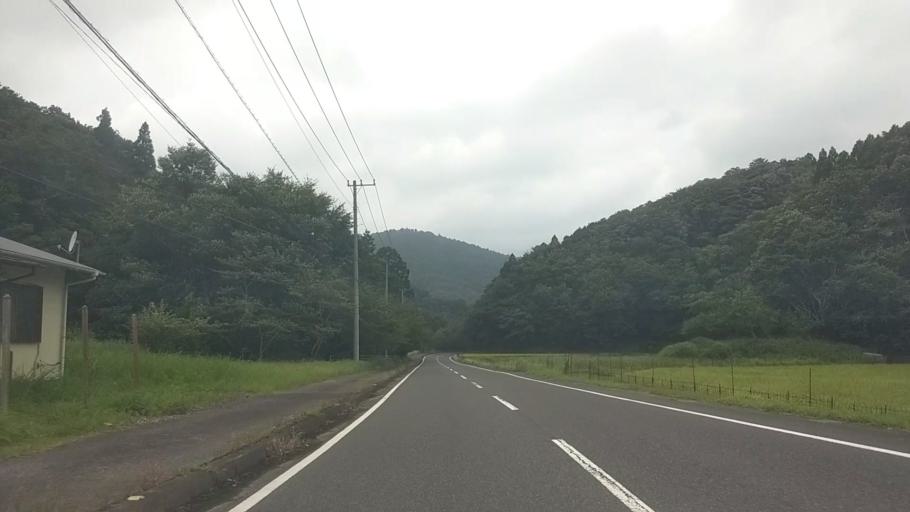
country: JP
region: Chiba
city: Kawaguchi
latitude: 35.2491
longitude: 140.0393
